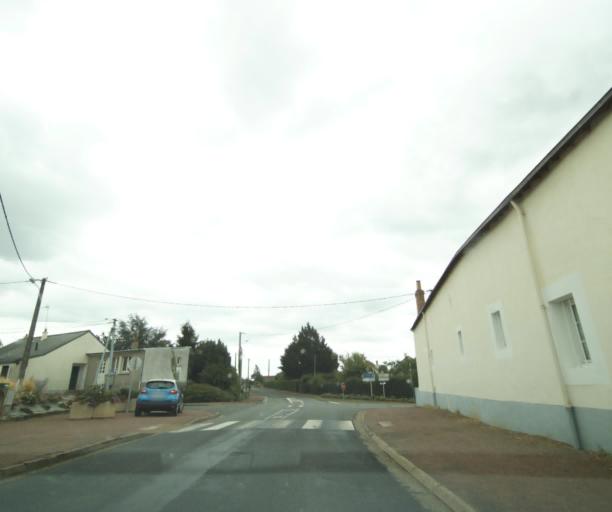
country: FR
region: Pays de la Loire
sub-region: Departement de la Sarthe
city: Precigne
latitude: 47.7643
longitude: -0.3198
